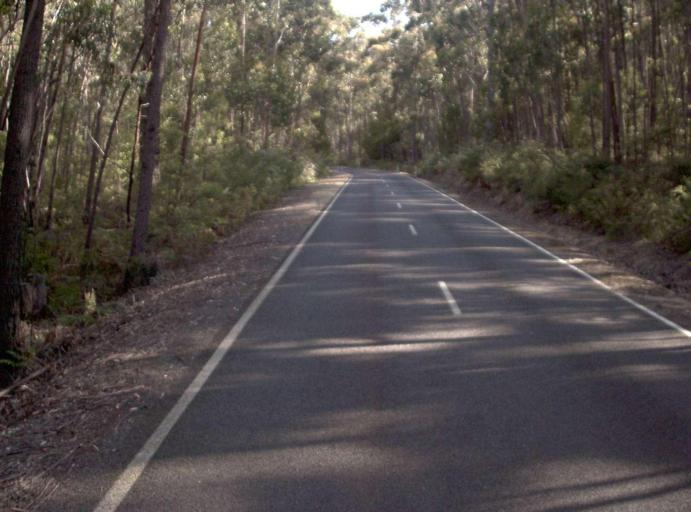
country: AU
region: Victoria
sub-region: East Gippsland
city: Lakes Entrance
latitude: -37.5955
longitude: 148.5286
